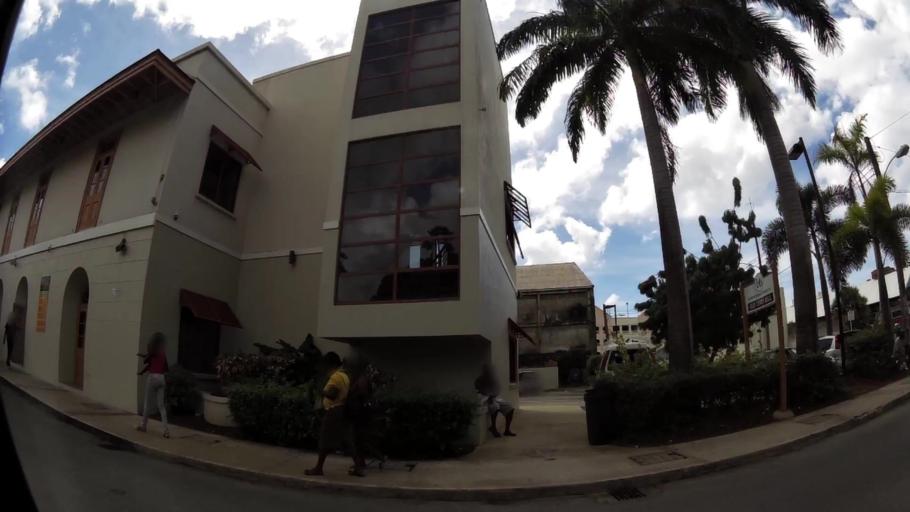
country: BB
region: Saint Michael
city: Bridgetown
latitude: 13.0981
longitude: -59.6191
